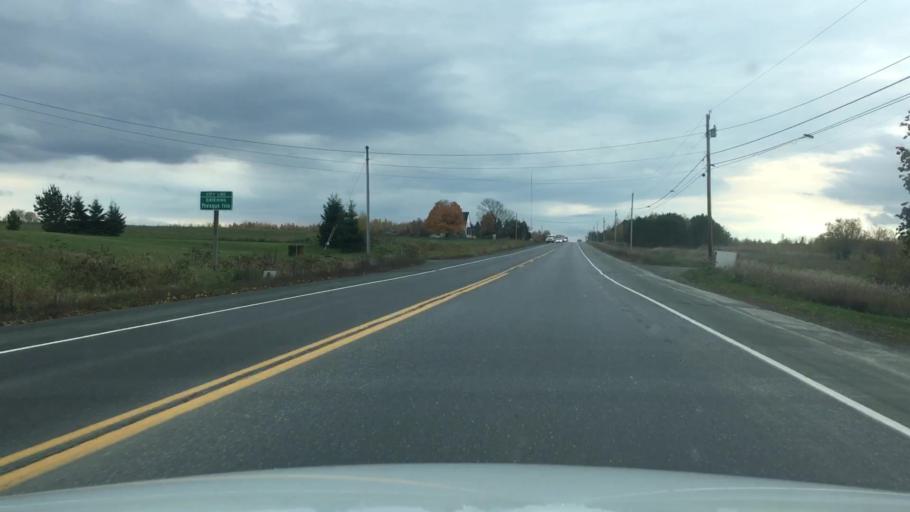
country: US
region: Maine
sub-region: Aroostook County
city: Caribou
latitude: 46.7776
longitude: -67.9893
